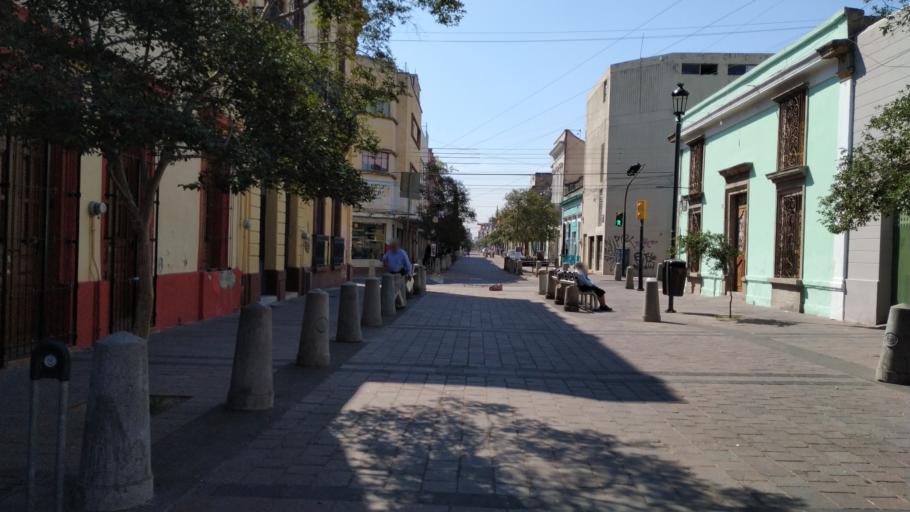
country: MX
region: Jalisco
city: Guadalajara
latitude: 20.6831
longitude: -103.3486
